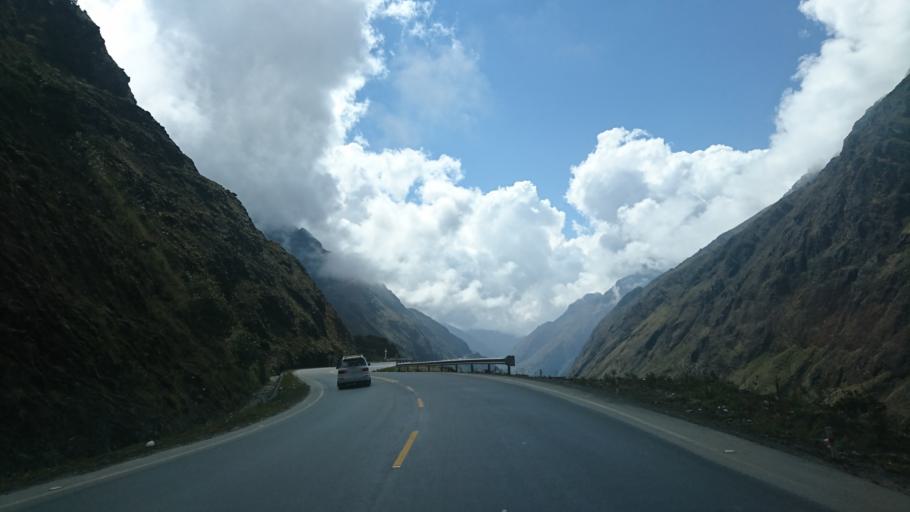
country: BO
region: La Paz
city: Coroico
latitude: -16.3199
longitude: -67.9313
